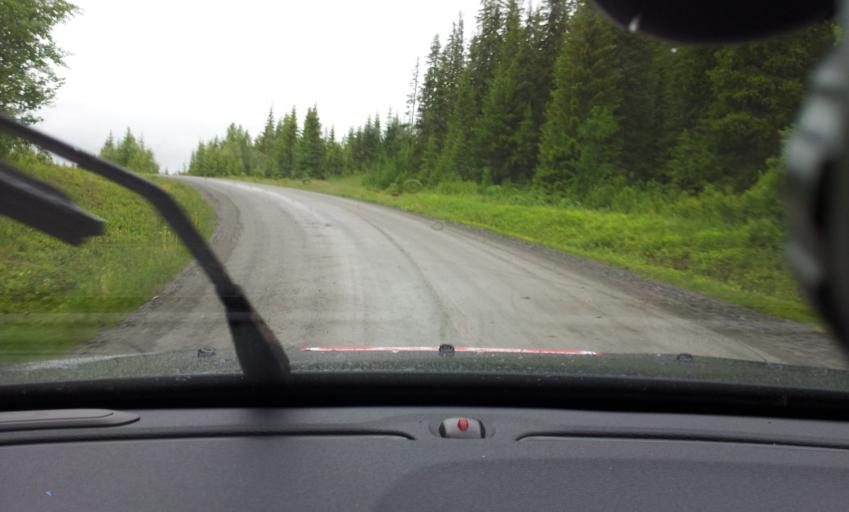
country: SE
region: Jaemtland
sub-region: Are Kommun
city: Are
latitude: 63.4207
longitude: 12.8235
